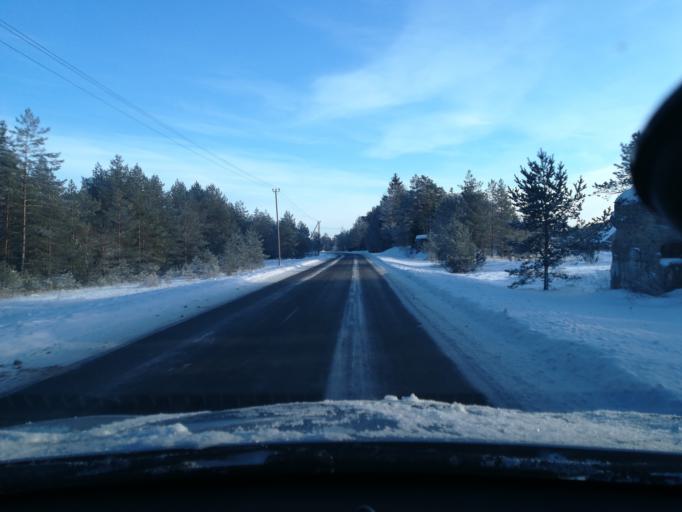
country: EE
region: Harju
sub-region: Keila linn
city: Keila
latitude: 59.3824
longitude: 24.4394
